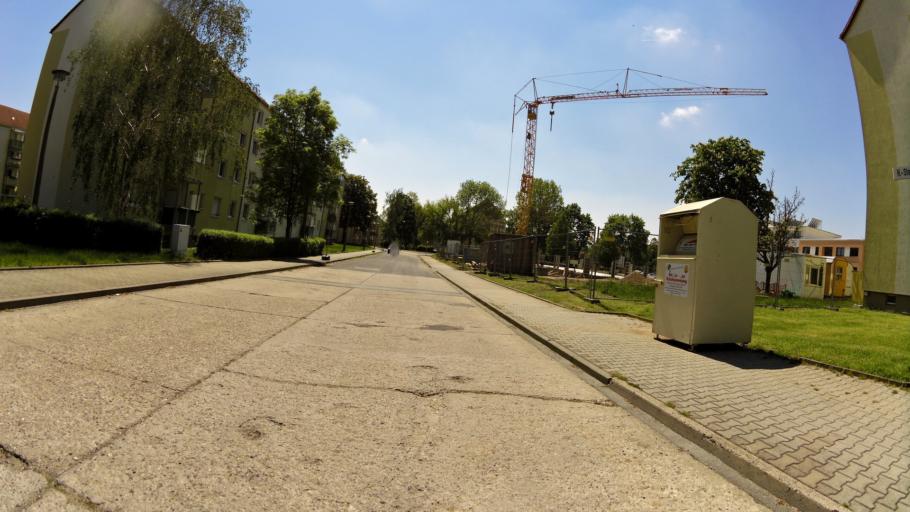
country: DE
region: Saxony
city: Riesa
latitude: 51.3211
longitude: 13.2580
